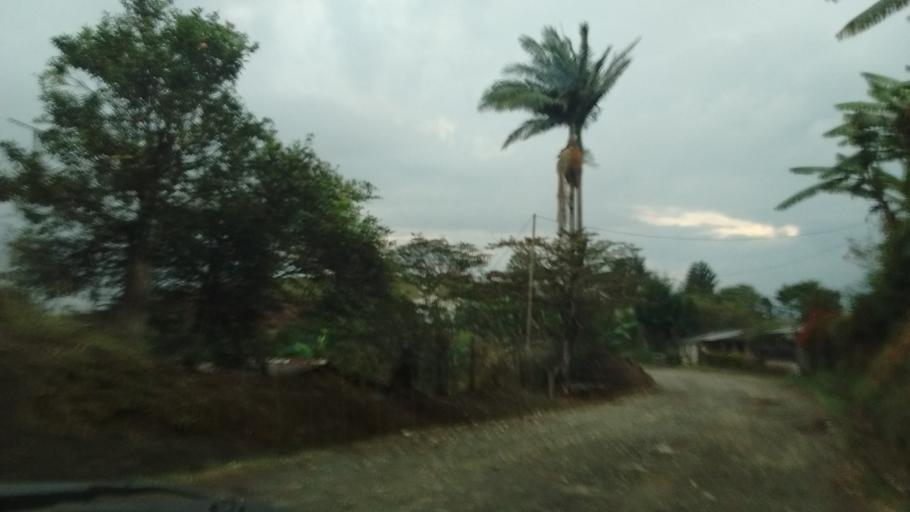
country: CO
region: Cauca
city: Lopez
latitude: 2.3946
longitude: -76.7426
